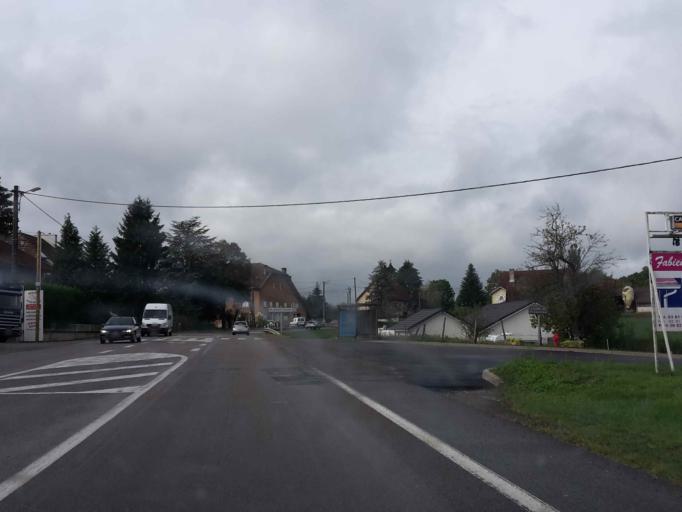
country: FR
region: Franche-Comte
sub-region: Departement du Doubs
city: Roulans
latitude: 47.3373
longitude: 6.2844
